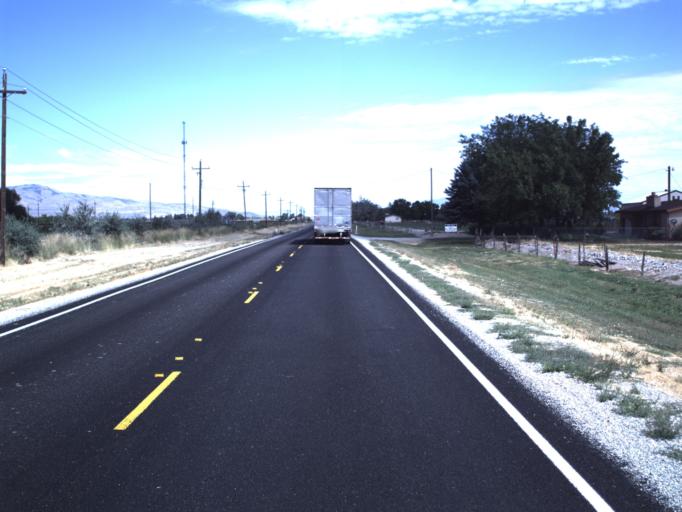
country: US
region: Utah
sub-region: Box Elder County
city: Honeyville
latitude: 41.6295
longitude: -112.1271
